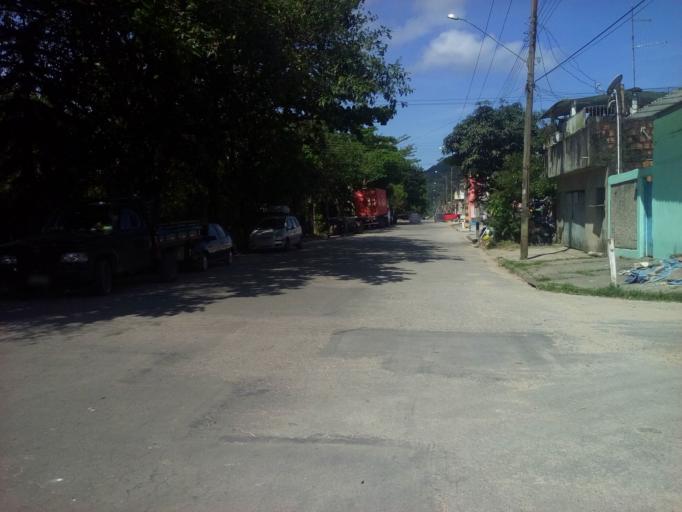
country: BR
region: Sao Paulo
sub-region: Guaruja
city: Guaruja
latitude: -23.9608
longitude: -46.2542
